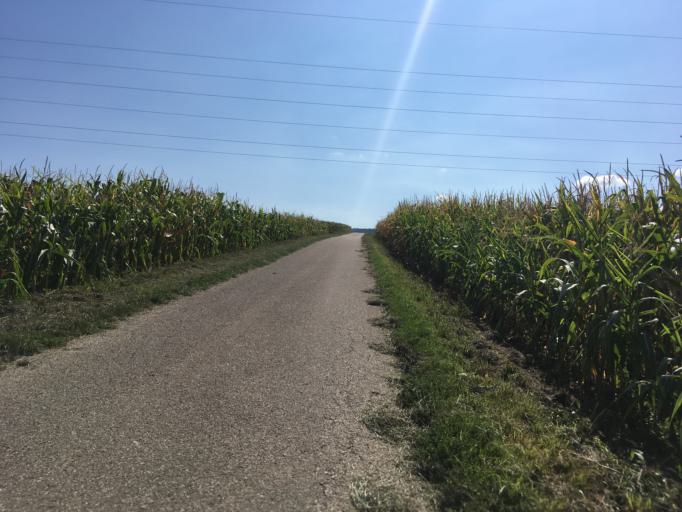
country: DE
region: Baden-Wuerttemberg
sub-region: Regierungsbezirk Stuttgart
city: Guglingen
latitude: 49.0624
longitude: 9.0199
